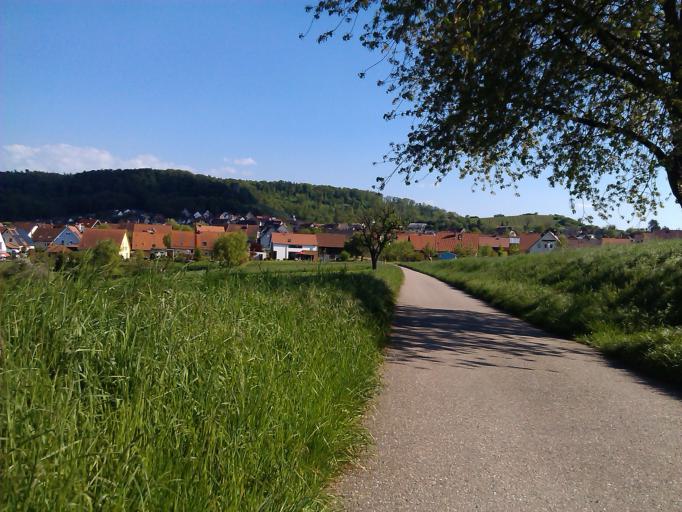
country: DE
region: Baden-Wuerttemberg
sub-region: Karlsruhe Region
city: Sternenfels
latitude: 49.0571
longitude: 8.8465
